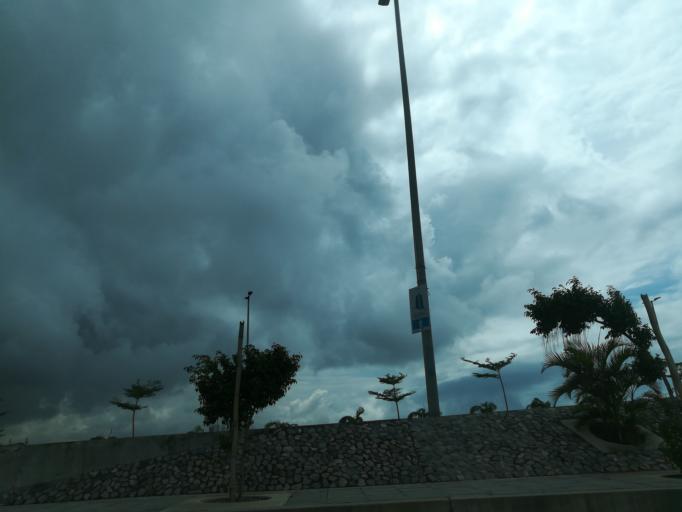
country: NG
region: Lagos
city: Lagos
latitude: 6.4199
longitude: 3.4135
